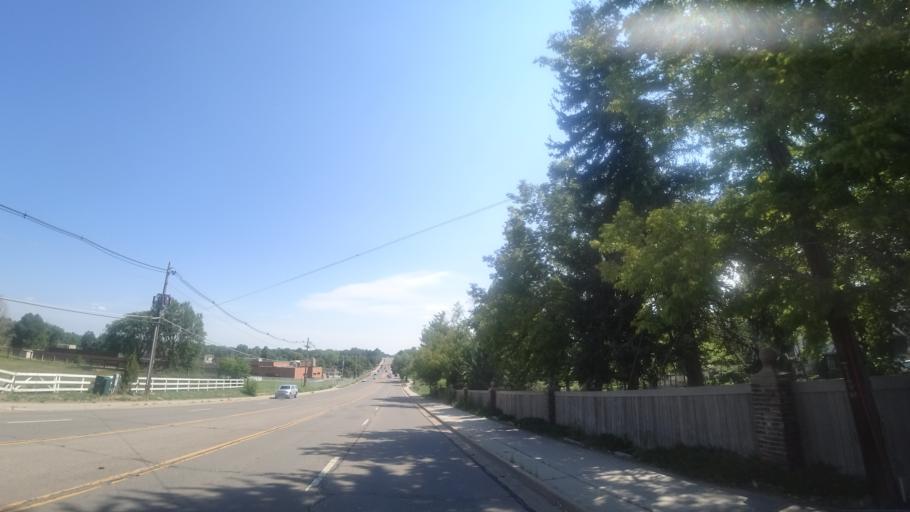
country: US
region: Colorado
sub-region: Arapahoe County
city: Cherry Hills Village
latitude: 39.6407
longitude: -104.9597
